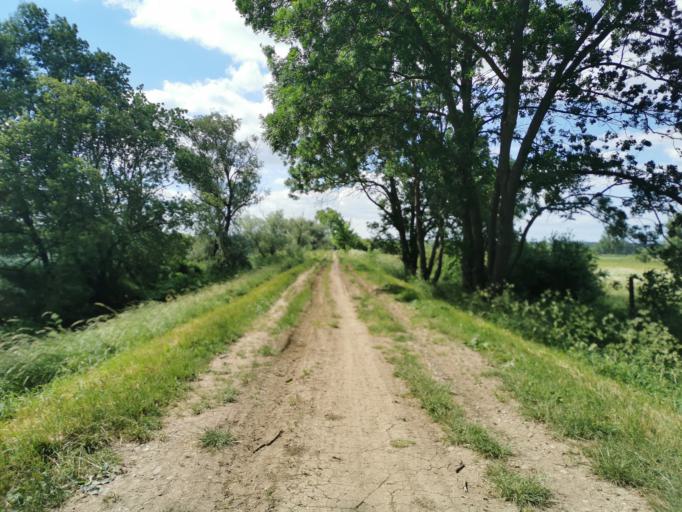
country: CZ
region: South Moravian
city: Rohatec
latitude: 48.8748
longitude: 17.2093
